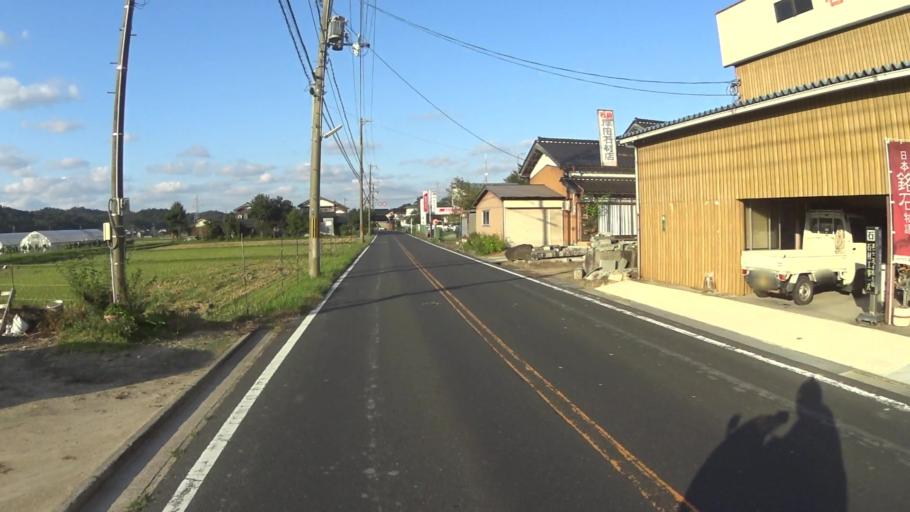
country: JP
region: Kyoto
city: Miyazu
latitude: 35.5986
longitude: 135.0455
